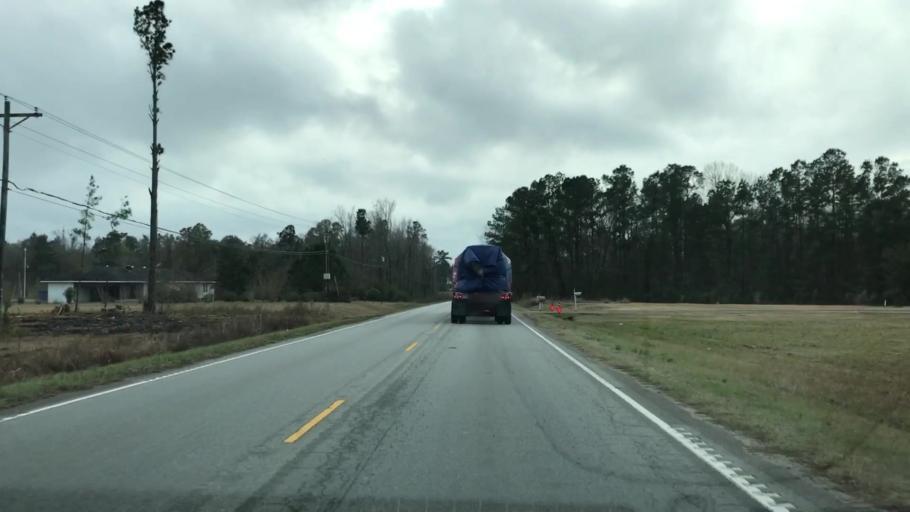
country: US
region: South Carolina
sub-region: Berkeley County
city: Moncks Corner
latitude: 33.2341
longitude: -79.9487
